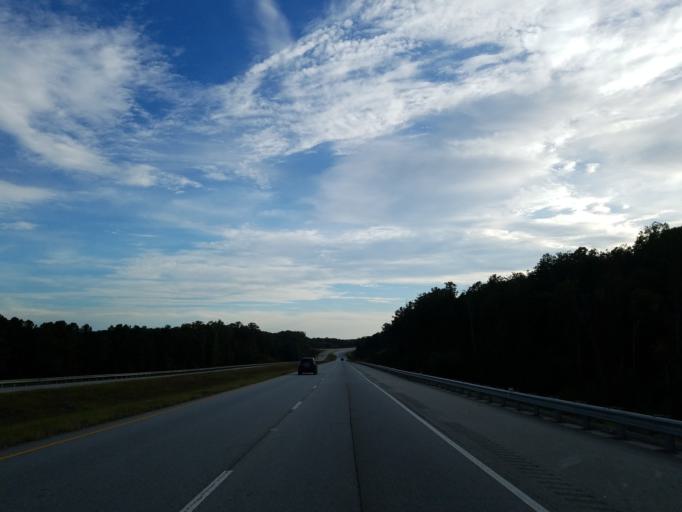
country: US
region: Georgia
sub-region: Bartow County
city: Emerson
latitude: 34.1263
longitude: -84.7651
